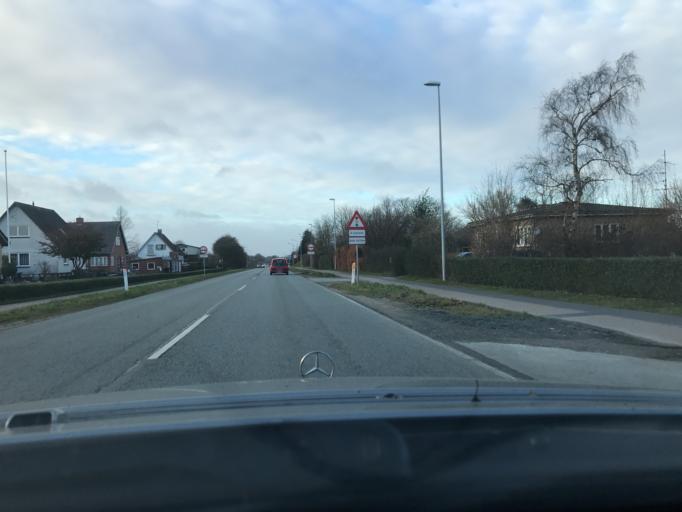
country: DK
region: South Denmark
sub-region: Sonderborg Kommune
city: Nordborg
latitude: 55.0474
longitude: 9.7814
